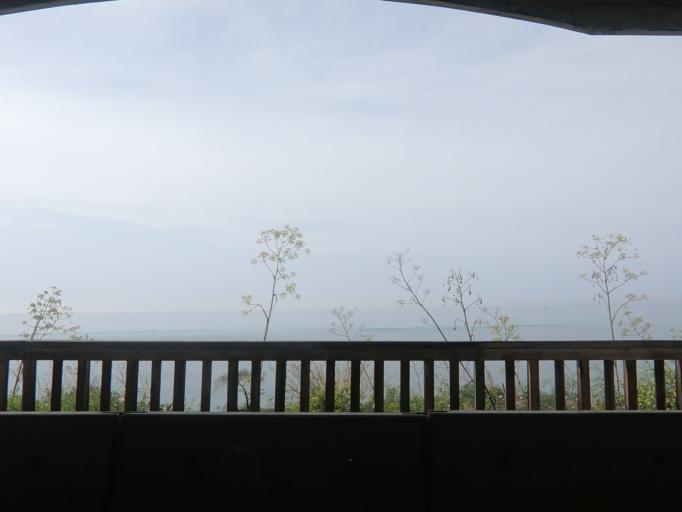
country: PT
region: Setubal
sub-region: Setubal
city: Setubal
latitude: 38.4851
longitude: -8.9521
